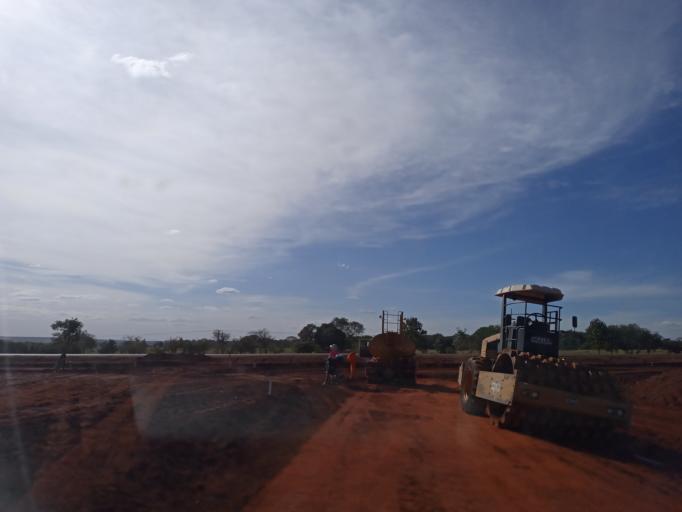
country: BR
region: Minas Gerais
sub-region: Ituiutaba
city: Ituiutaba
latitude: -18.9664
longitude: -49.5063
